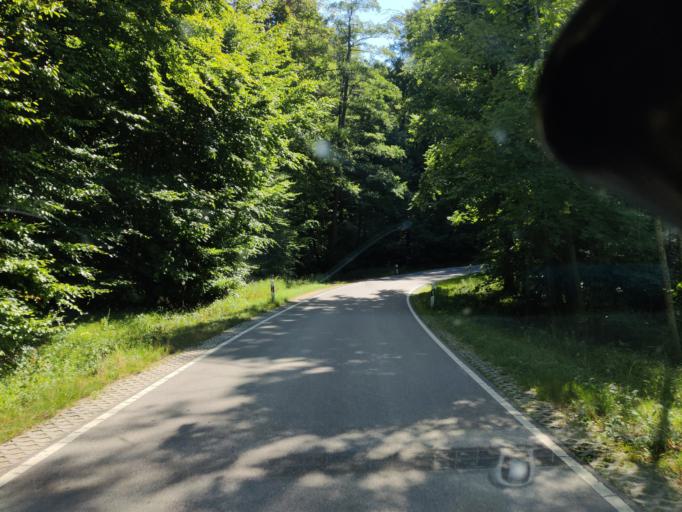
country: DE
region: Bavaria
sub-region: Regierungsbezirk Mittelfranken
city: Bergen
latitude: 49.0875
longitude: 11.1552
